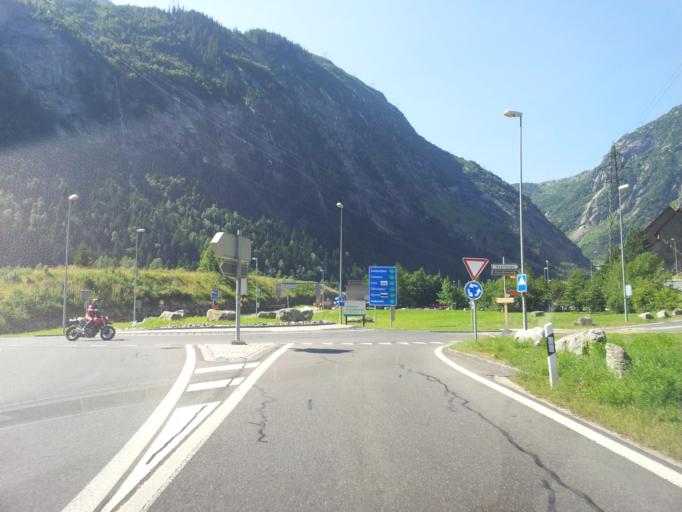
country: CH
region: Uri
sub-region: Uri
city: Andermatt
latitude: 46.6713
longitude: 8.5921
